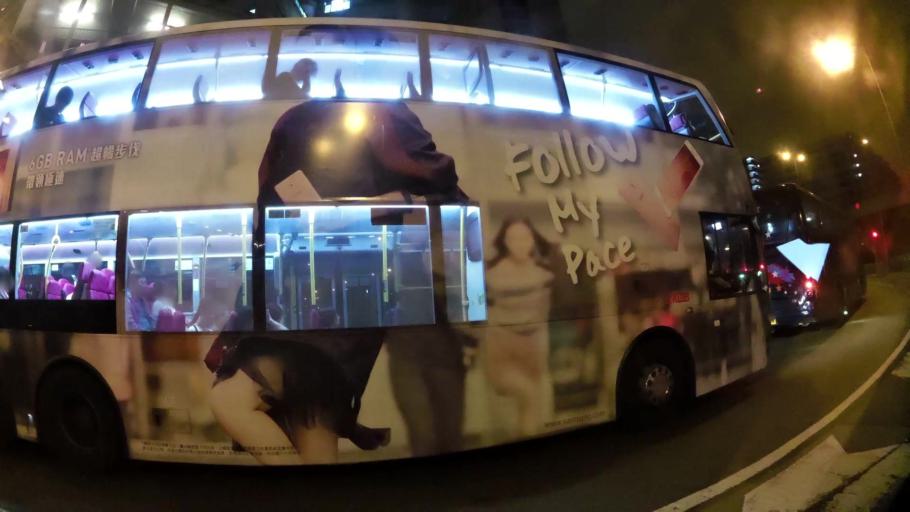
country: HK
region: Tsuen Wan
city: Tsuen Wan
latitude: 22.3559
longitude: 114.1237
